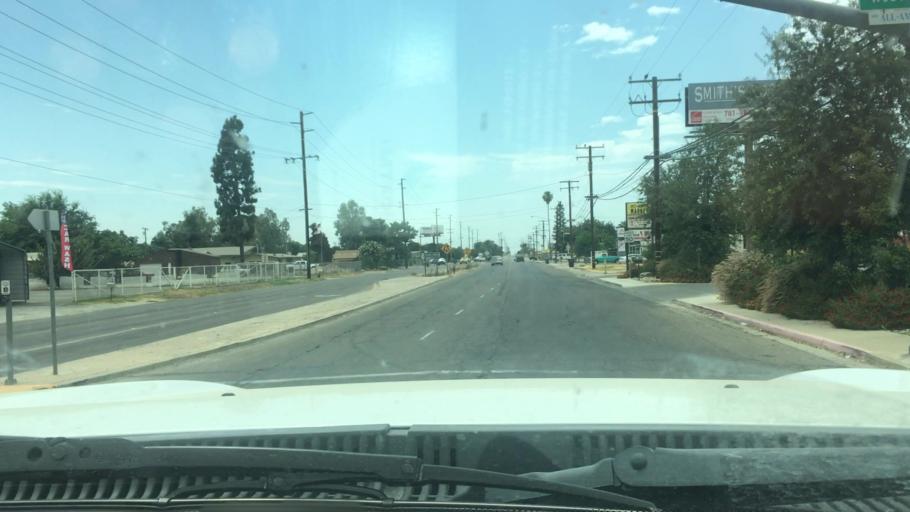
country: US
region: California
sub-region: Tulare County
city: Porterville
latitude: 36.0658
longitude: -119.0709
